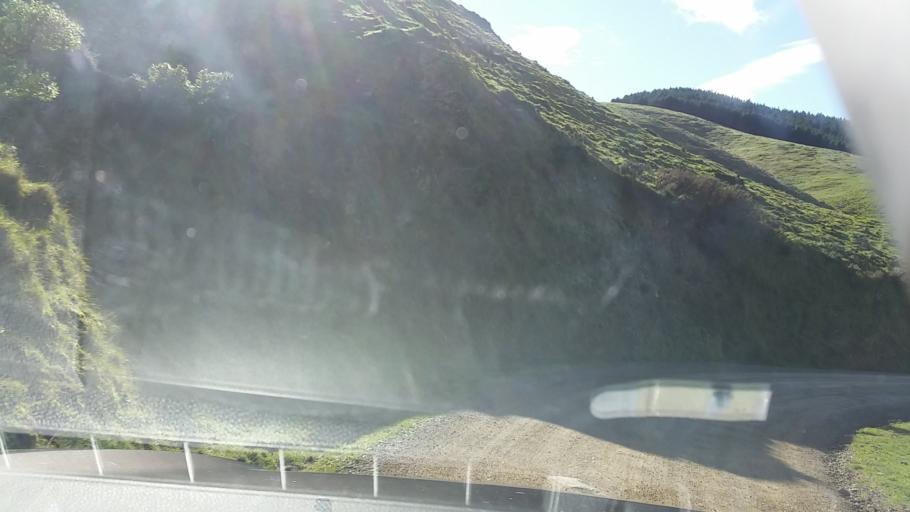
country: NZ
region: Marlborough
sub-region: Marlborough District
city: Picton
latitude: -40.9874
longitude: 173.8087
